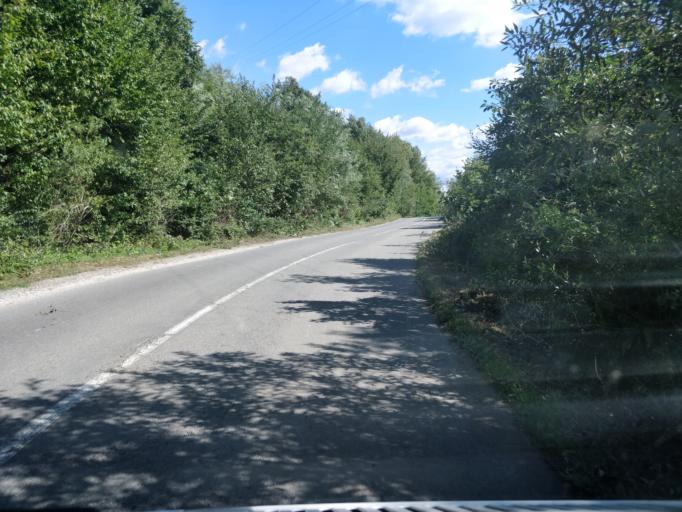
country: RO
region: Cluj
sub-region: Comuna Sacueu
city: Sacuieu
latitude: 46.8643
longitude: 22.8701
